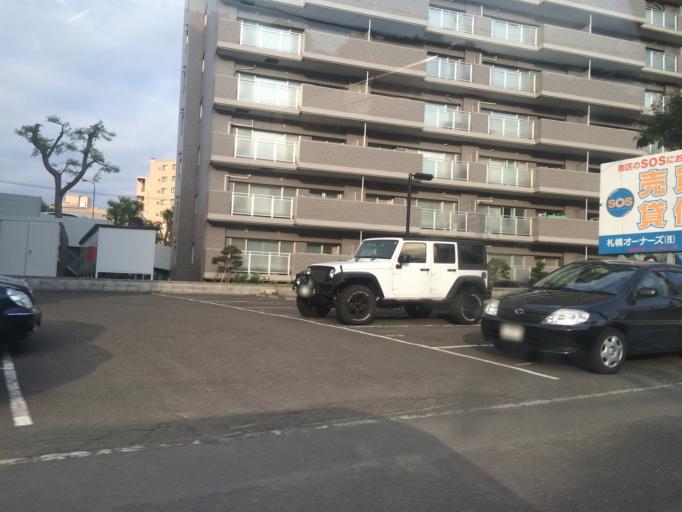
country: JP
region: Hokkaido
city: Sapporo
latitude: 42.9915
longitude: 141.3506
